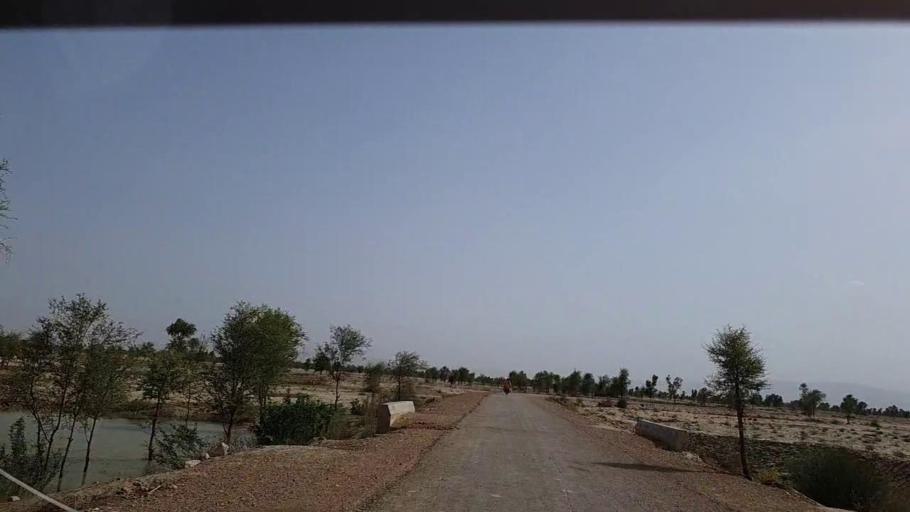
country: PK
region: Sindh
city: Johi
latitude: 26.6223
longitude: 67.4995
